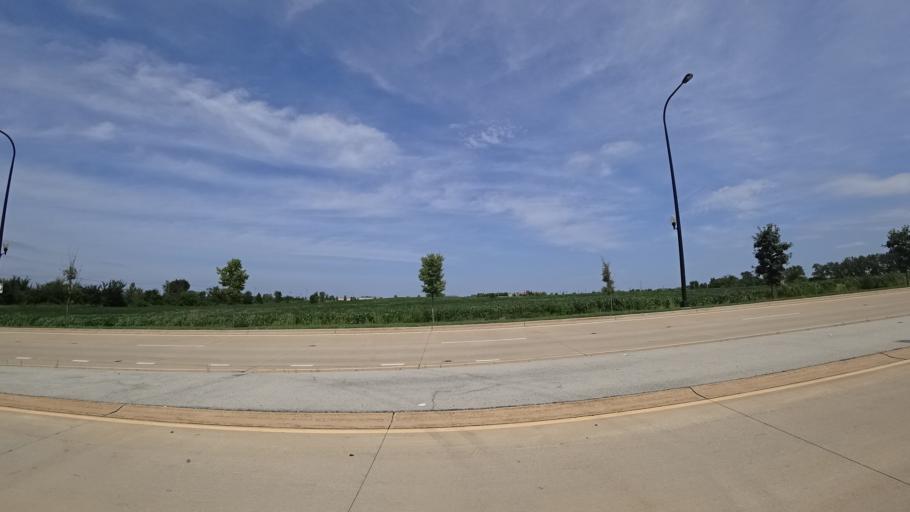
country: US
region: Illinois
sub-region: Cook County
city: Orland Hills
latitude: 41.5604
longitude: -87.8501
